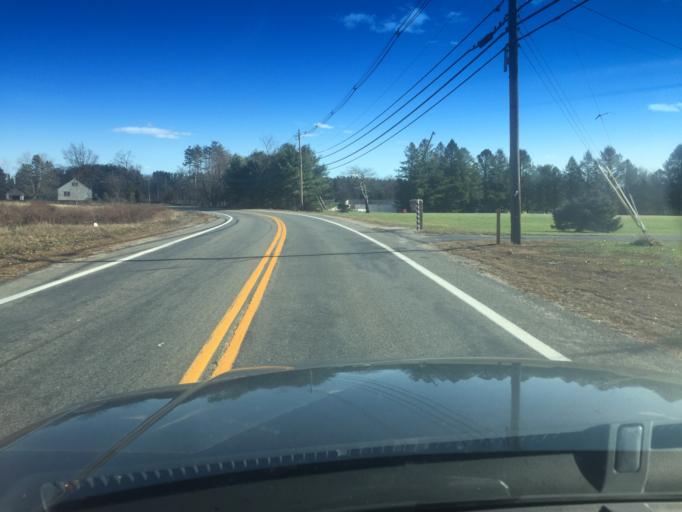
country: US
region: Rhode Island
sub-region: Providence County
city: Greenville
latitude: 41.8639
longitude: -71.5798
